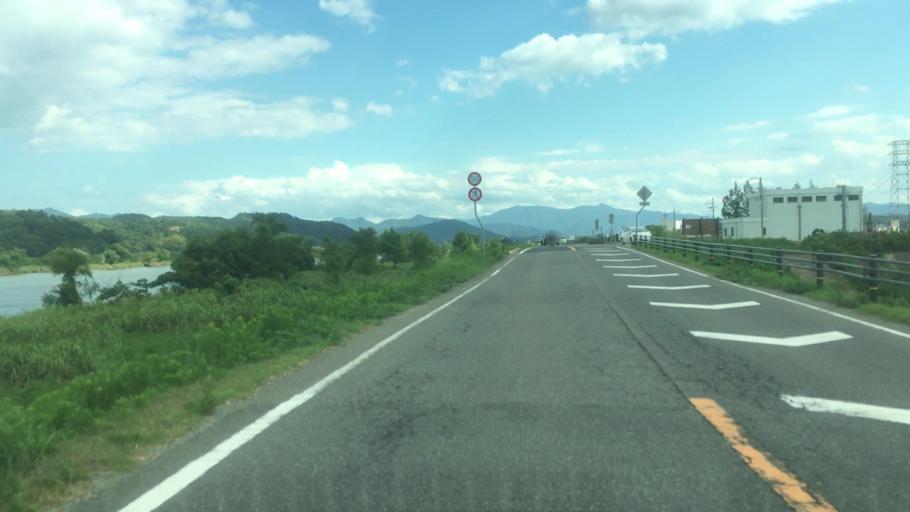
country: JP
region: Hyogo
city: Toyooka
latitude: 35.5741
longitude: 134.8063
